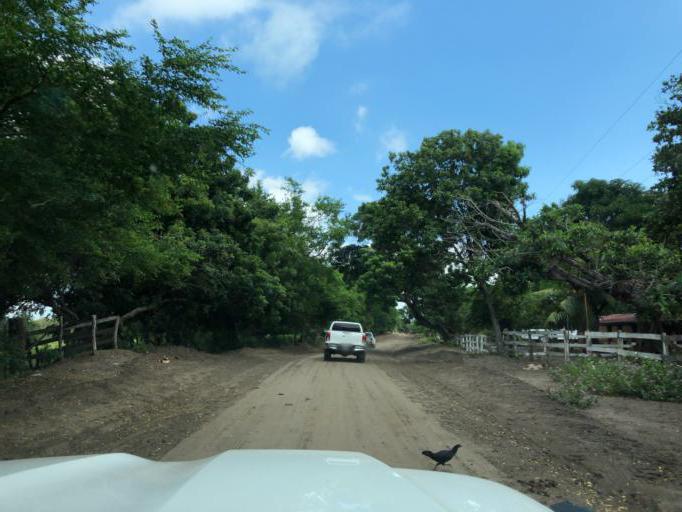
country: NI
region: Granada
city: Granada
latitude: 12.0032
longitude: -85.9346
